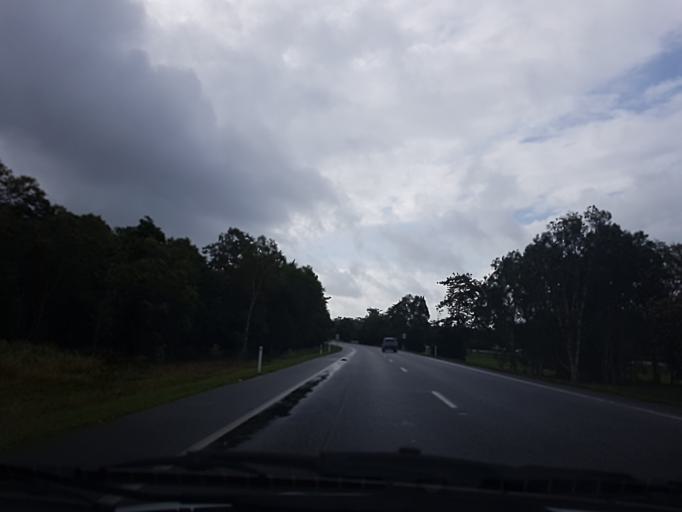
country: AU
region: Queensland
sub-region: Cairns
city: Trinity Beach
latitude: -16.8103
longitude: 145.6925
